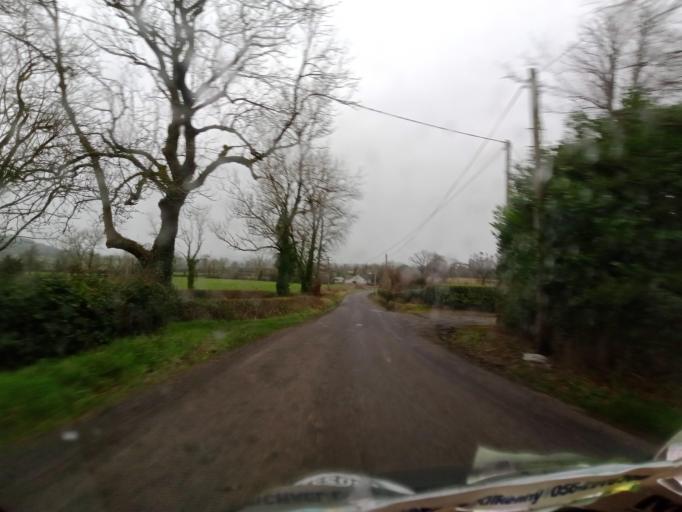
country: IE
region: Munster
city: Fethard
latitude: 52.5559
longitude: -7.7642
